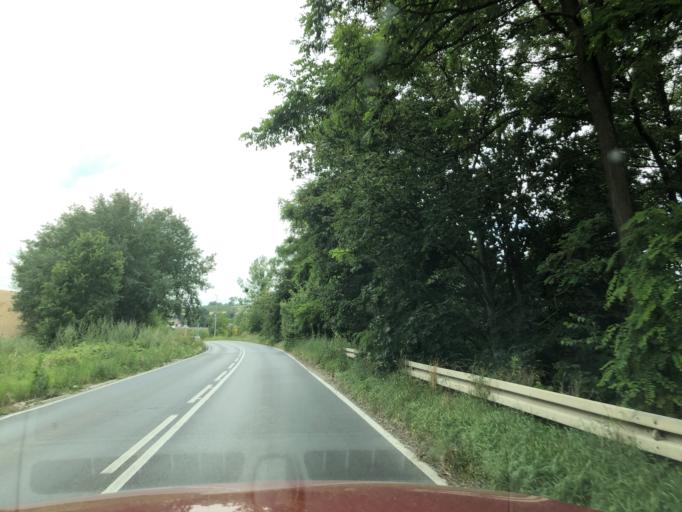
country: PL
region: Lower Silesian Voivodeship
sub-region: Powiat trzebnicki
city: Trzebnica
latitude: 51.2926
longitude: 17.0465
